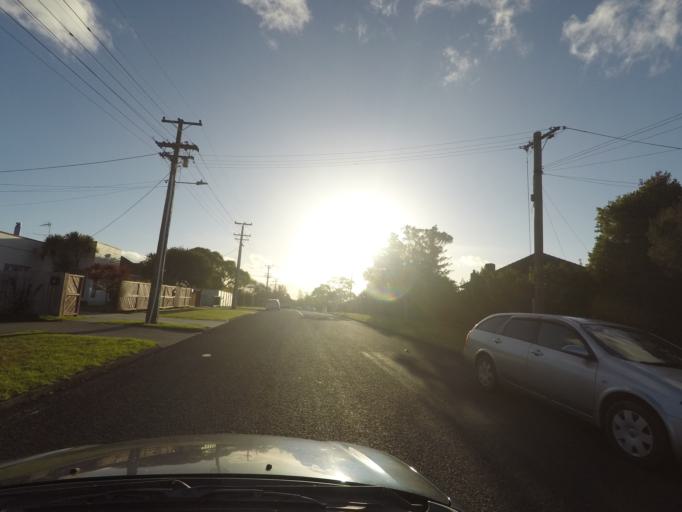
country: NZ
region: Auckland
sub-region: Auckland
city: Waitakere
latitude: -36.9015
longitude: 174.6736
